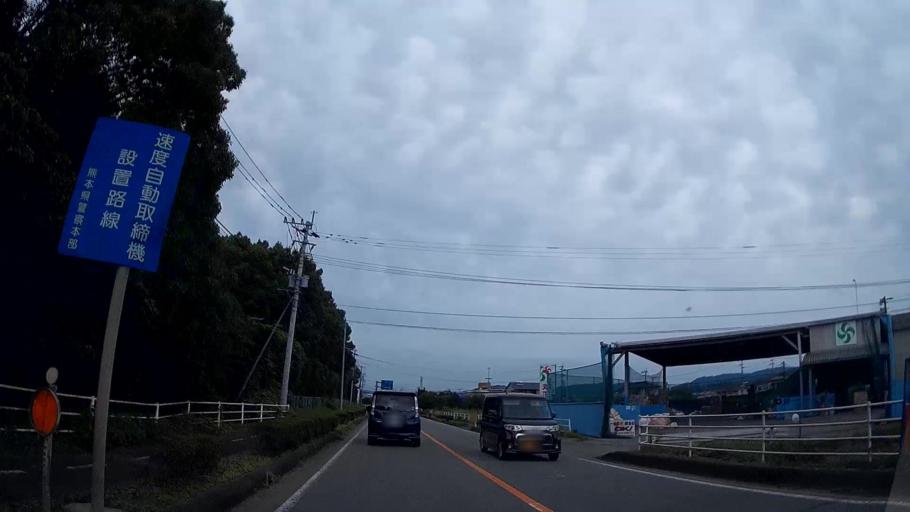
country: JP
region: Kumamoto
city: Kikuchi
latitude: 32.9592
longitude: 130.8195
